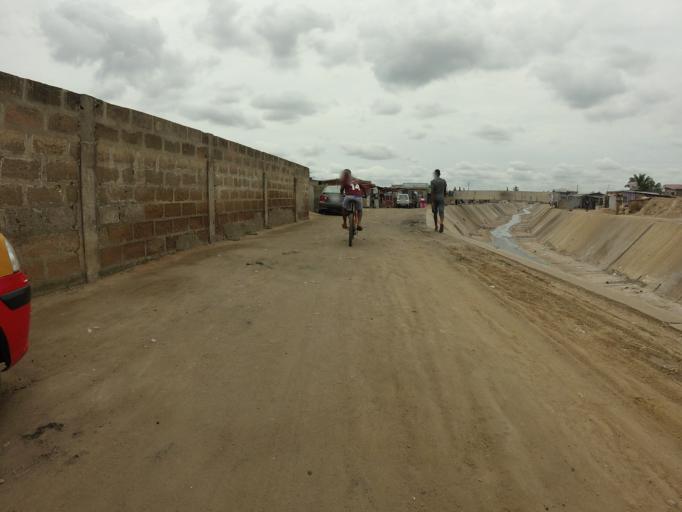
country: GH
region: Greater Accra
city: Accra
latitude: 5.5929
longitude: -0.2140
